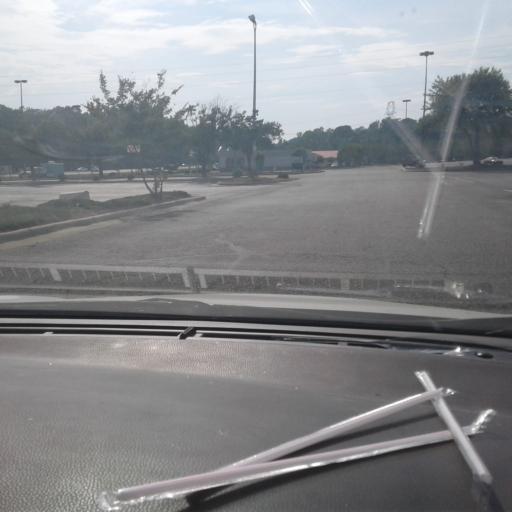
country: US
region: North Carolina
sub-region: Harnett County
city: Dunn
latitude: 35.3220
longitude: -78.6368
